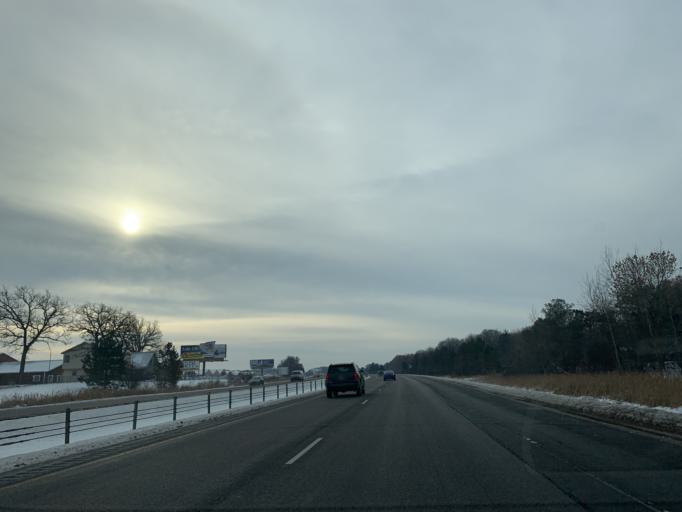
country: US
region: Minnesota
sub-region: Chisago County
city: Wyoming
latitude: 45.3321
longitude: -93.0049
